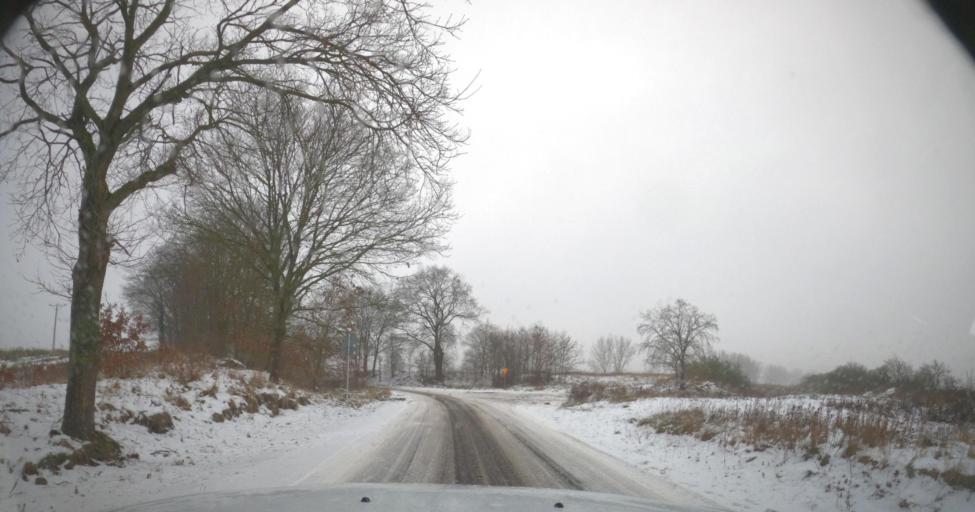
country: PL
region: West Pomeranian Voivodeship
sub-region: Powiat gryficki
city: Gryfice
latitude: 53.8917
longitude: 15.1283
